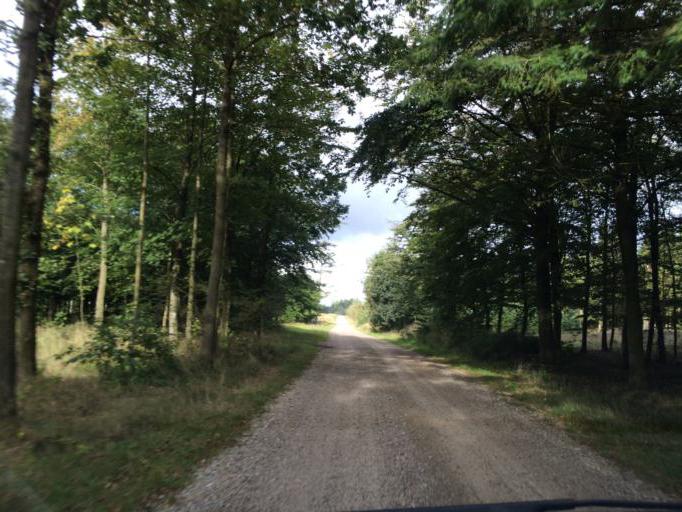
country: DK
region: Central Jutland
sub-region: Holstebro Kommune
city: Ulfborg
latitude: 56.2702
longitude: 8.4125
